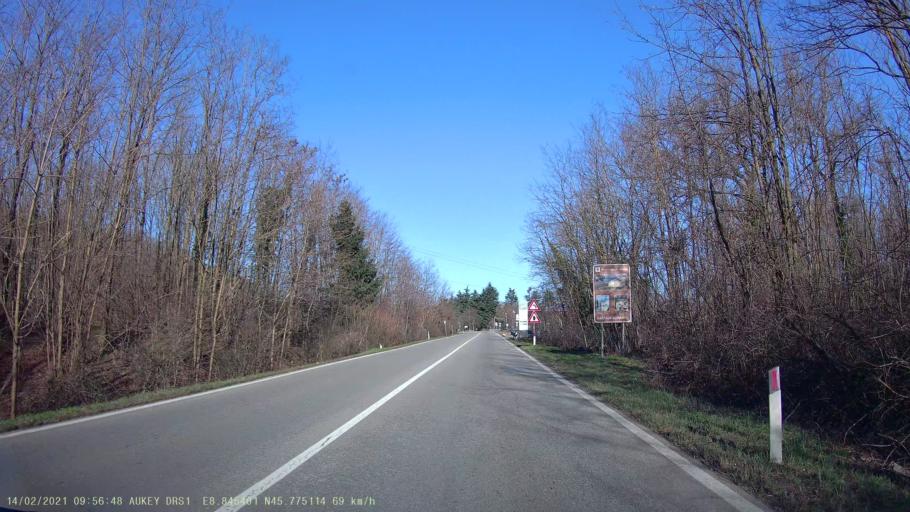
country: IT
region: Lombardy
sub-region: Provincia di Varese
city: Gazzada Schianno
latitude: 45.7755
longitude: 8.8450
